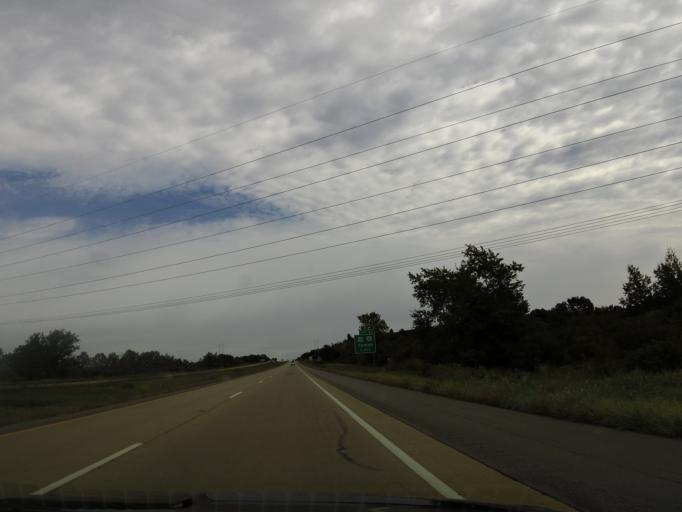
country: US
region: Wisconsin
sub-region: Monroe County
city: Tomah
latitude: 43.9617
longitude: -90.4953
